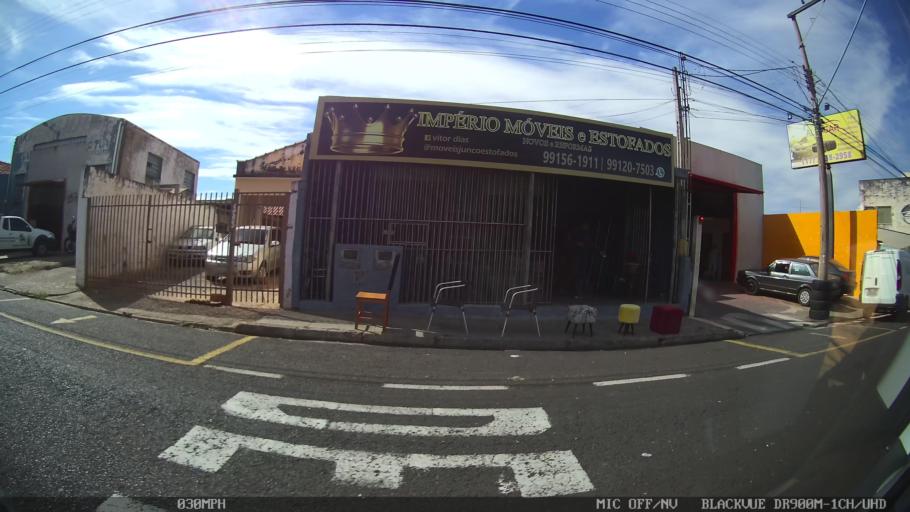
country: BR
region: Sao Paulo
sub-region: Sao Jose Do Rio Preto
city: Sao Jose do Rio Preto
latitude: -20.8216
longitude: -49.3547
